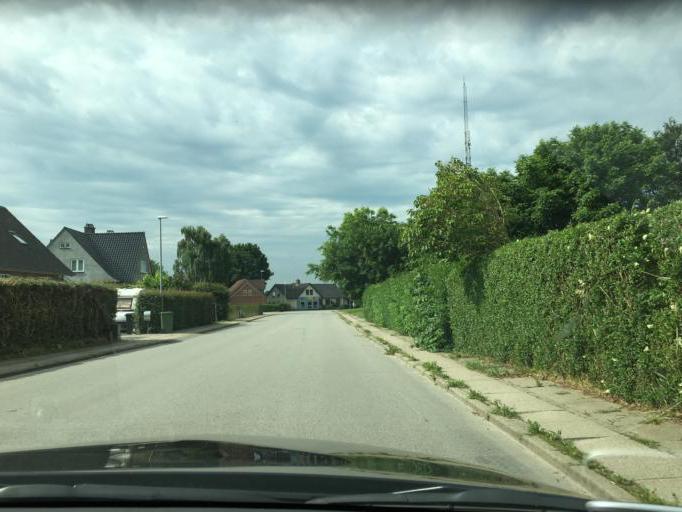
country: DK
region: South Denmark
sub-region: Vejle Kommune
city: Borkop
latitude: 55.6163
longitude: 9.5692
